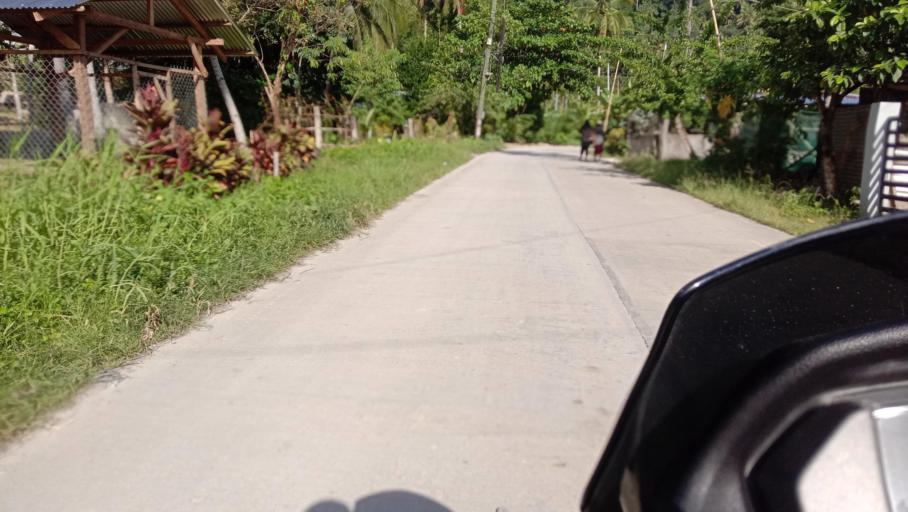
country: PH
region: Caraga
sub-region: Province of Agusan del Sur
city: Alegria
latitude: 8.4809
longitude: 125.9665
